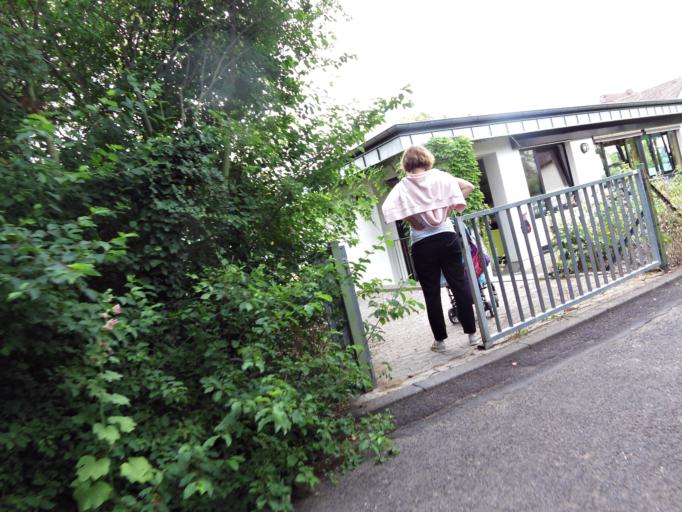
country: DE
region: Bavaria
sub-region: Regierungsbezirk Unterfranken
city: Wuerzburg
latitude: 49.7622
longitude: 9.9358
